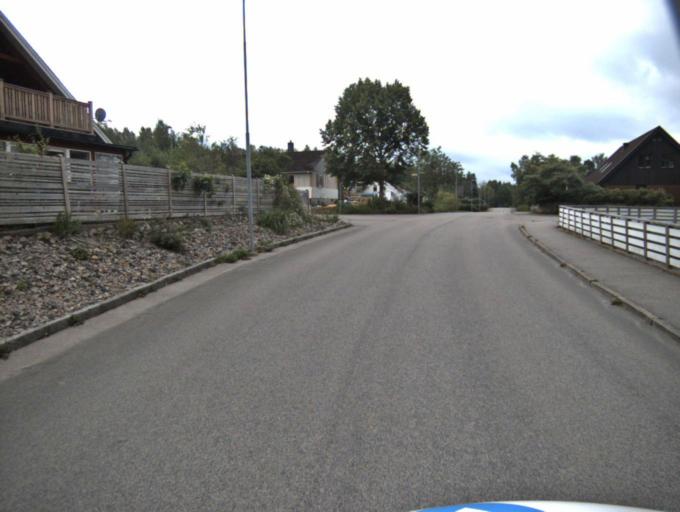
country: SE
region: Vaestra Goetaland
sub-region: Ulricehamns Kommun
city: Ulricehamn
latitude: 57.7790
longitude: 13.4152
